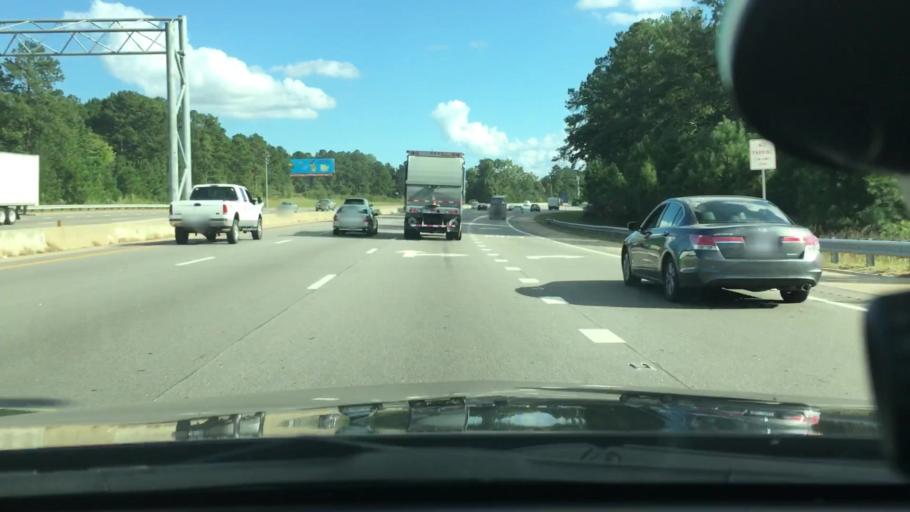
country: US
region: North Carolina
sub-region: Wake County
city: Raleigh
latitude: 35.7903
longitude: -78.5768
